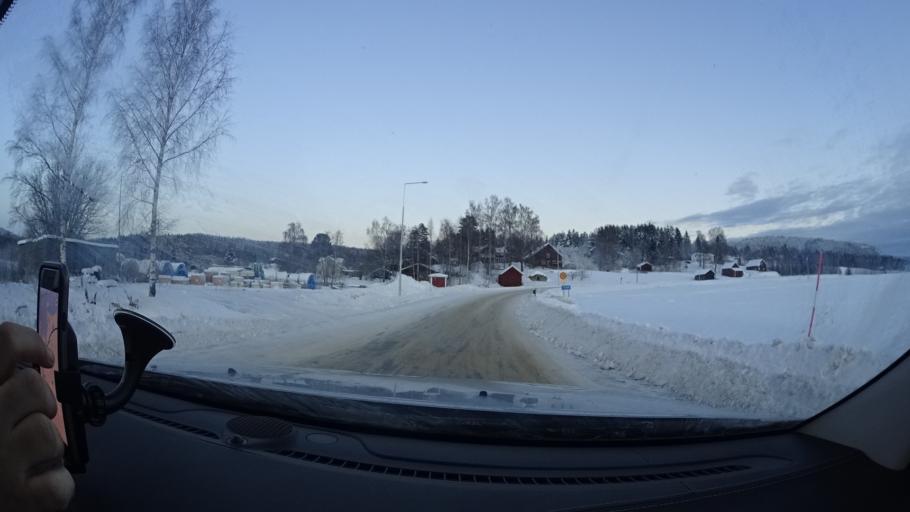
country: SE
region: Vaesternorrland
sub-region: Timra Kommun
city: Timra
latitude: 62.5671
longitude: 17.1168
